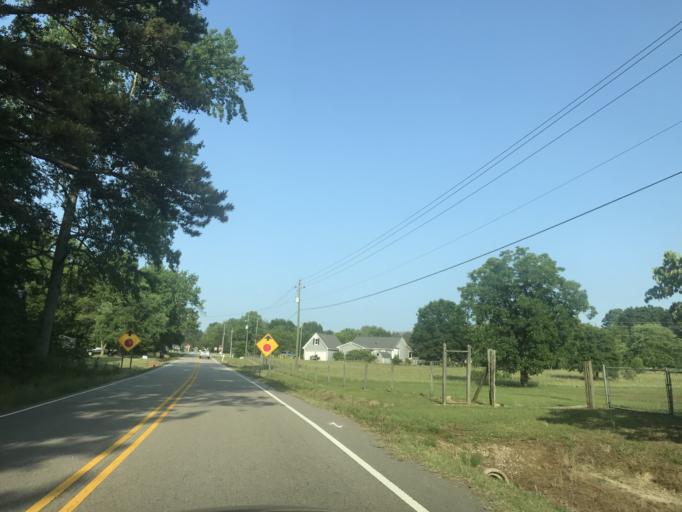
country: US
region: North Carolina
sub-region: Wake County
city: Rolesville
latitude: 35.8612
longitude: -78.4850
